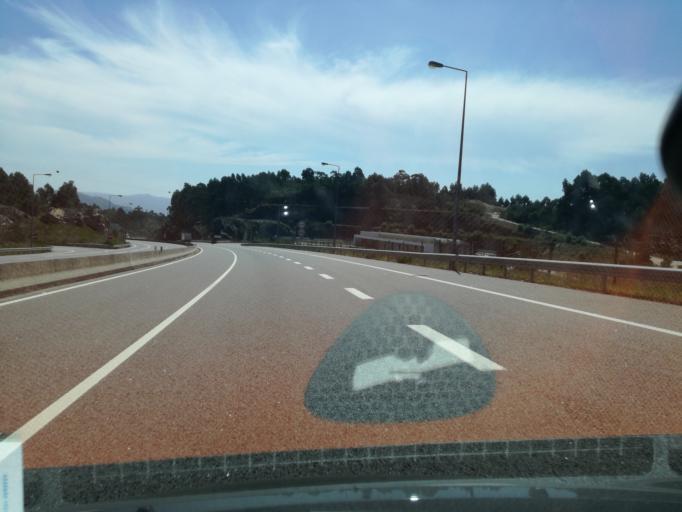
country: PT
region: Viana do Castelo
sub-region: Viana do Castelo
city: Meadela
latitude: 41.7436
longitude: -8.7978
